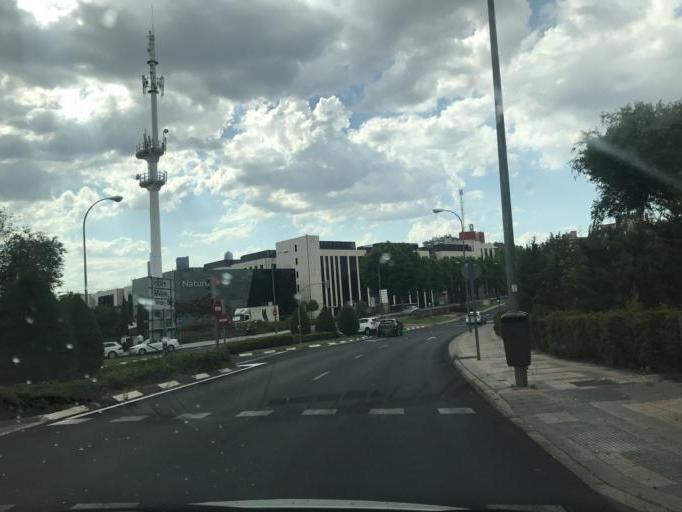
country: ES
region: Madrid
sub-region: Provincia de Madrid
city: Pinar de Chamartin
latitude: 40.4726
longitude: -3.6621
